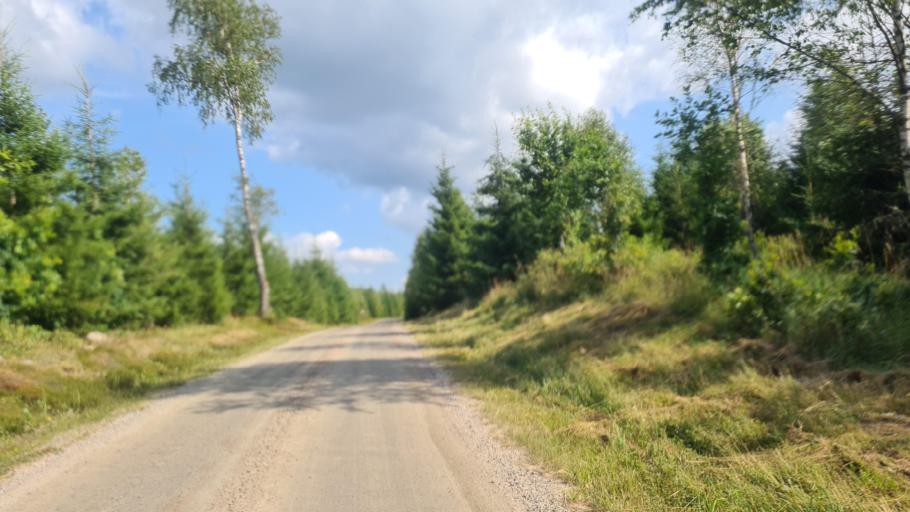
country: SE
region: Kronoberg
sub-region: Ljungby Kommun
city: Ljungby
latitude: 56.7284
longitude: 13.8799
